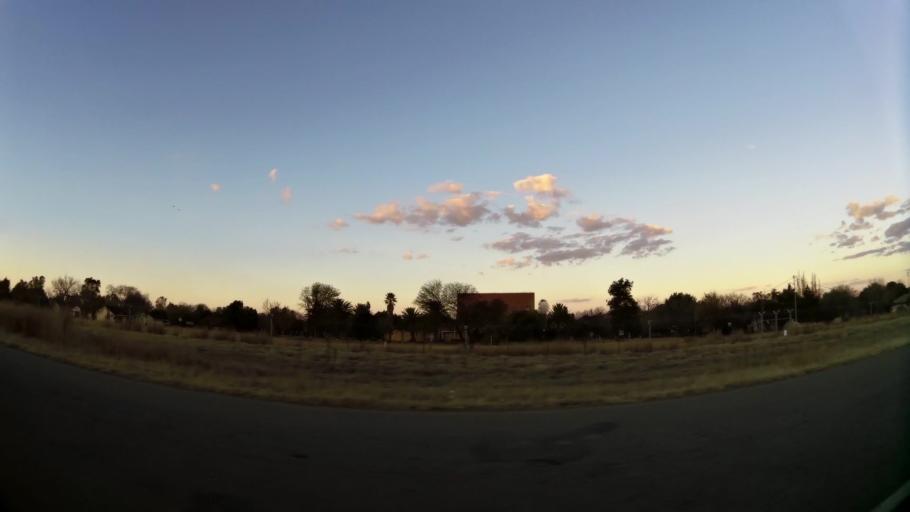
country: ZA
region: North-West
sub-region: Dr Kenneth Kaunda District Municipality
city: Potchefstroom
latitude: -26.6802
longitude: 27.0751
